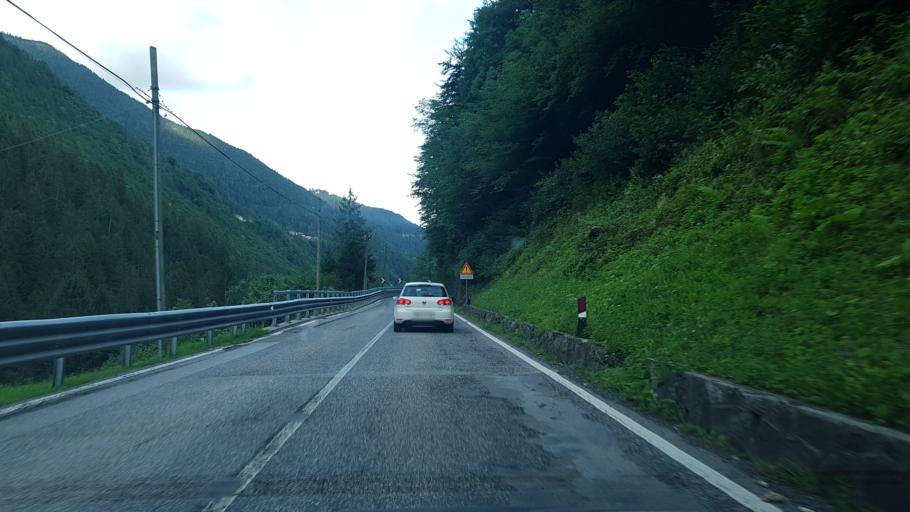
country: IT
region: Friuli Venezia Giulia
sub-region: Provincia di Udine
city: Rigolato
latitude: 46.5633
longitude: 12.8429
